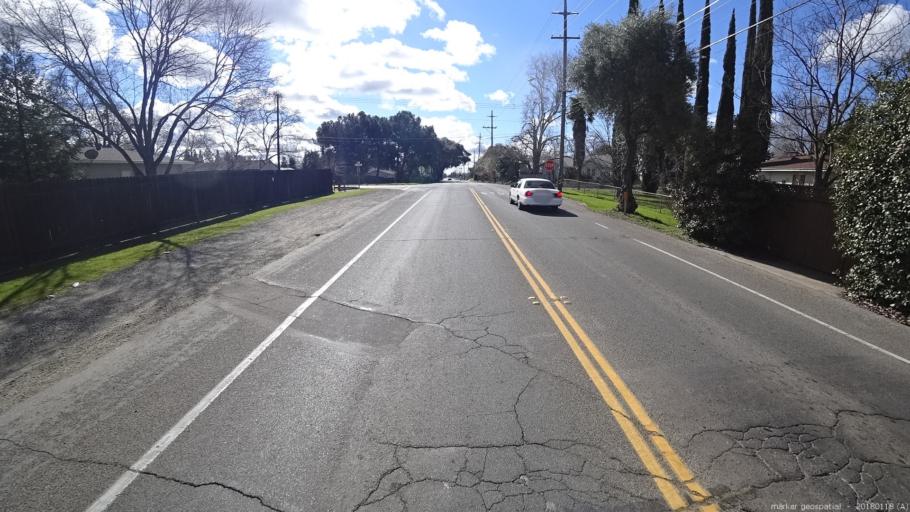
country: US
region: California
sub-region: Sacramento County
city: Orangevale
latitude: 38.6858
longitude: -121.2021
